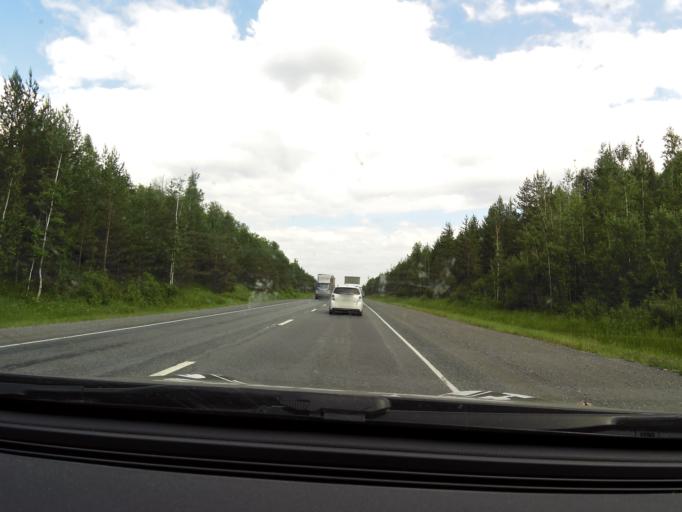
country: RU
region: Sverdlovsk
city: Nizhniye Sergi
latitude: 56.8250
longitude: 59.2452
